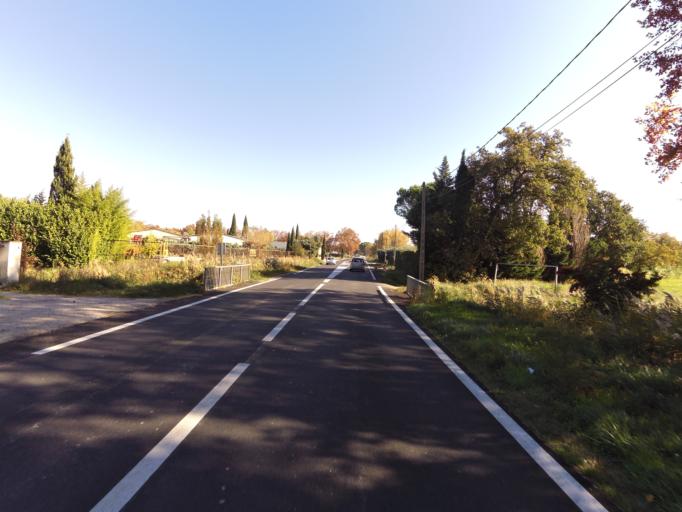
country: FR
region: Provence-Alpes-Cote d'Azur
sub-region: Departement du Vaucluse
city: Loriol-du-Comtat
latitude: 44.0784
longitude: 4.9886
